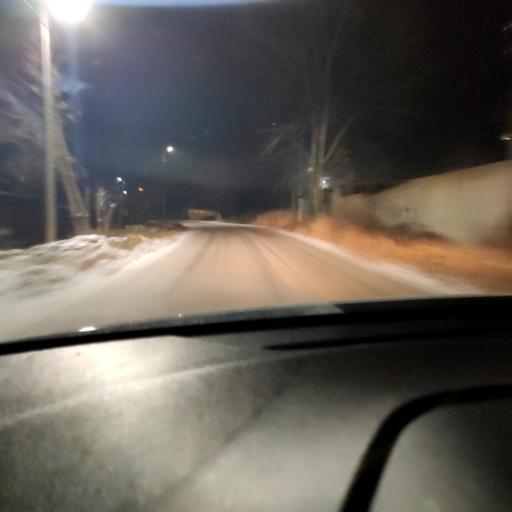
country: RU
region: Tatarstan
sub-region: Gorod Kazan'
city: Kazan
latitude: 55.7222
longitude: 49.0983
